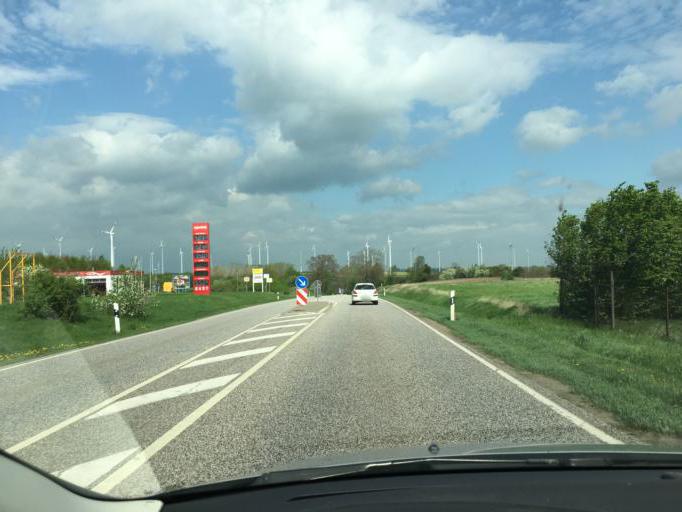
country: DE
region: Saxony-Anhalt
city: Alsleben
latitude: 51.7046
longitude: 11.6666
